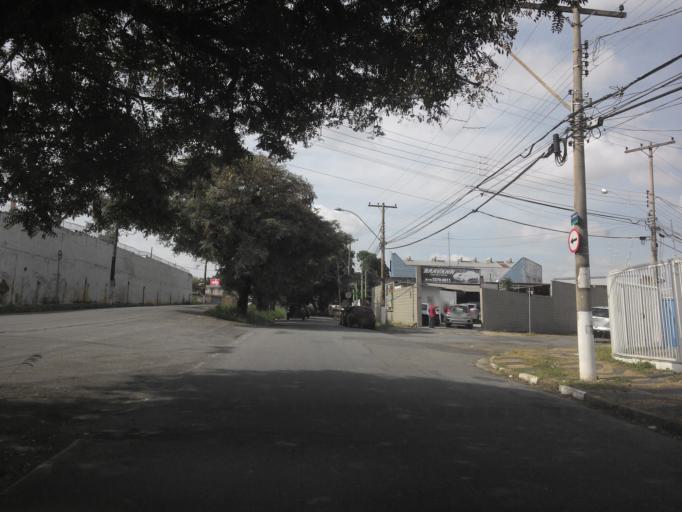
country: BR
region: Sao Paulo
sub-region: Campinas
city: Campinas
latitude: -22.9284
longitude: -47.0444
